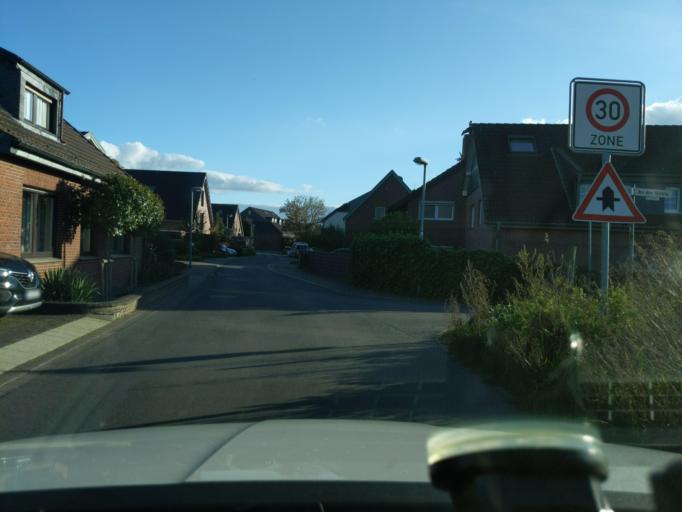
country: DE
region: North Rhine-Westphalia
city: Kempen
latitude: 51.3878
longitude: 6.4516
